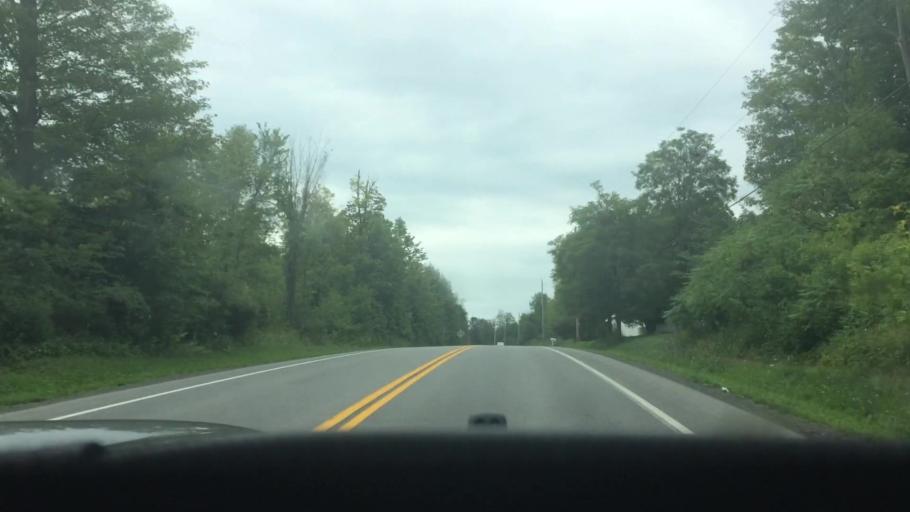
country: US
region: New York
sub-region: St. Lawrence County
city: Canton
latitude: 44.5170
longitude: -75.3386
